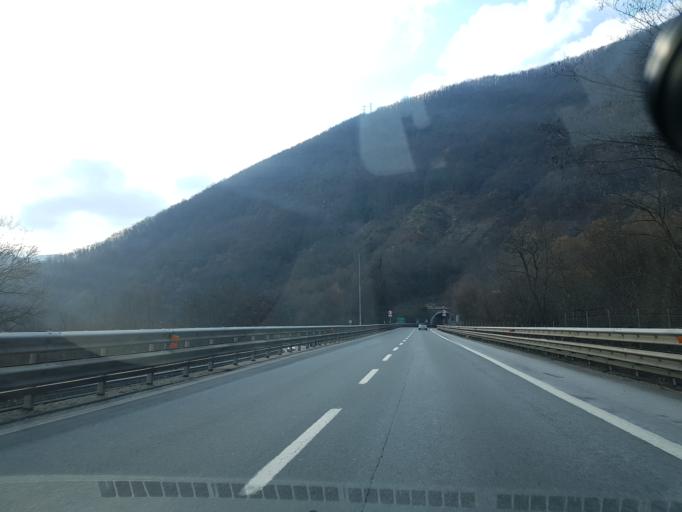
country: IT
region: Liguria
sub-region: Provincia di Genova
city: Isola del Cantone
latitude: 44.6657
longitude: 8.9308
